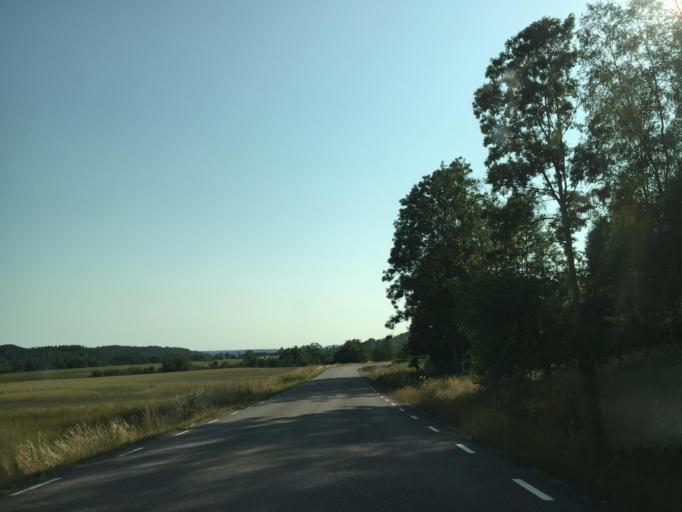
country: SE
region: Vaestra Goetaland
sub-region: Trollhattan
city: Sjuntorp
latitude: 58.2401
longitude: 12.1888
